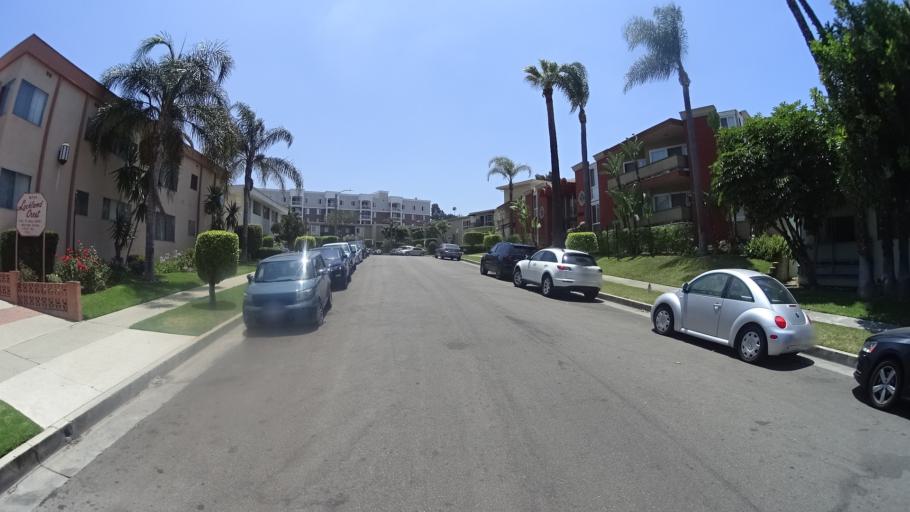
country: US
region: California
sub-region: Los Angeles County
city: View Park-Windsor Hills
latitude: 34.0086
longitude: -118.3401
